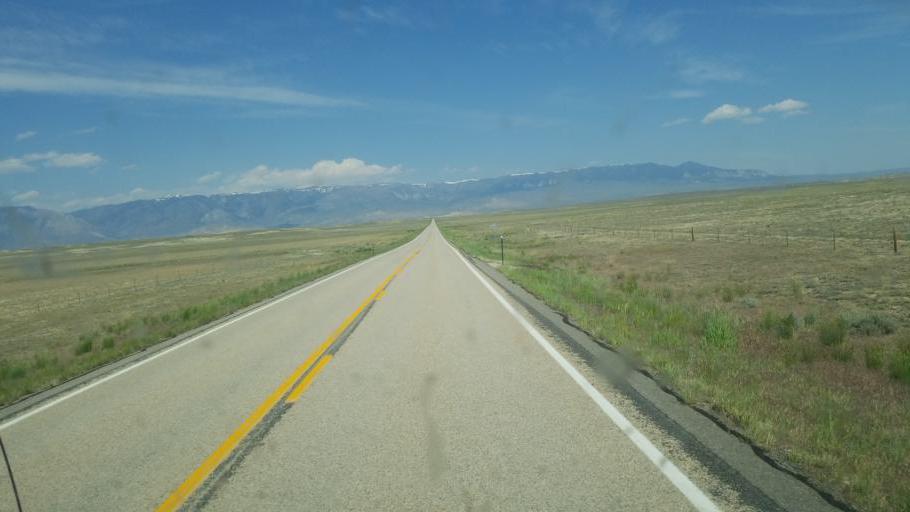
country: US
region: Wyoming
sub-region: Park County
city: Powell
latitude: 44.8587
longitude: -109.0227
